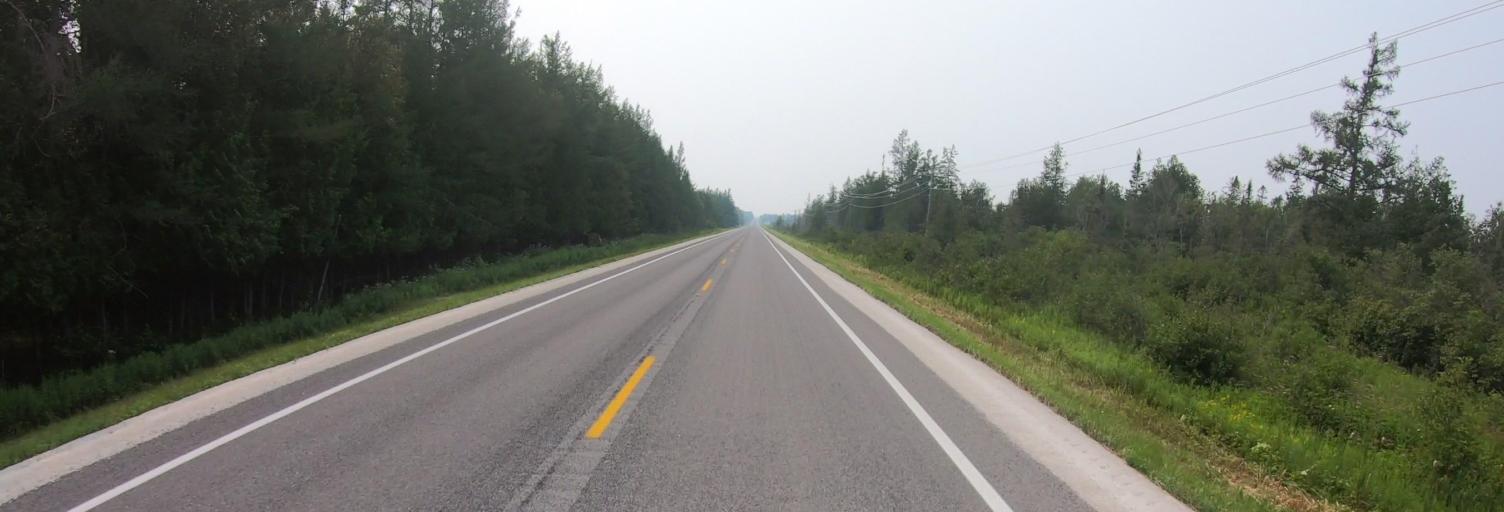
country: US
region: Michigan
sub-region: Chippewa County
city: Sault Ste. Marie
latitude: 46.0719
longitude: -84.1945
